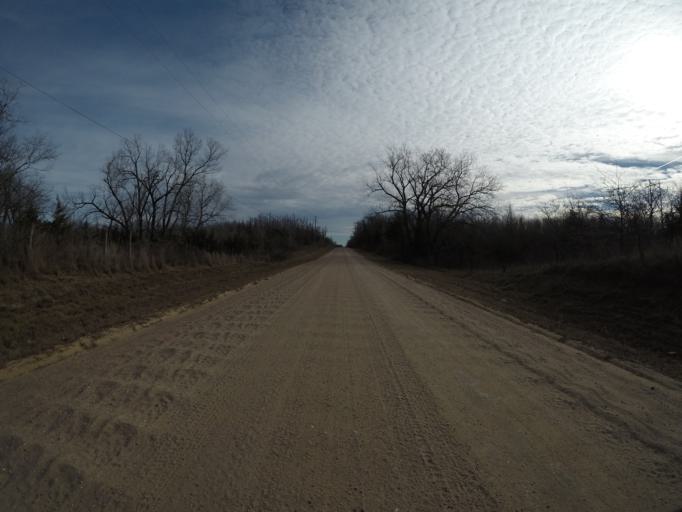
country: US
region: Kansas
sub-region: Reno County
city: Hutchinson
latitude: 38.1011
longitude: -97.8601
